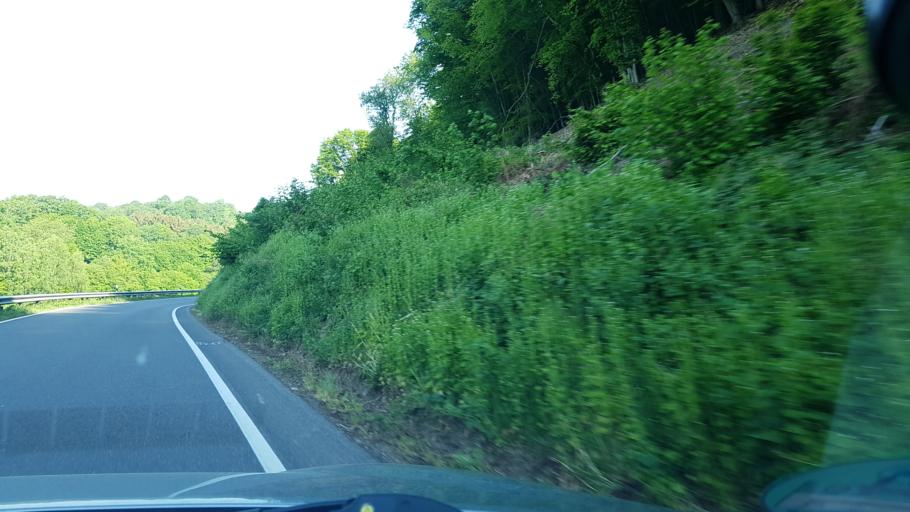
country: DE
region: Rheinland-Pfalz
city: Kadenbach
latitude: 50.3790
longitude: 7.7367
